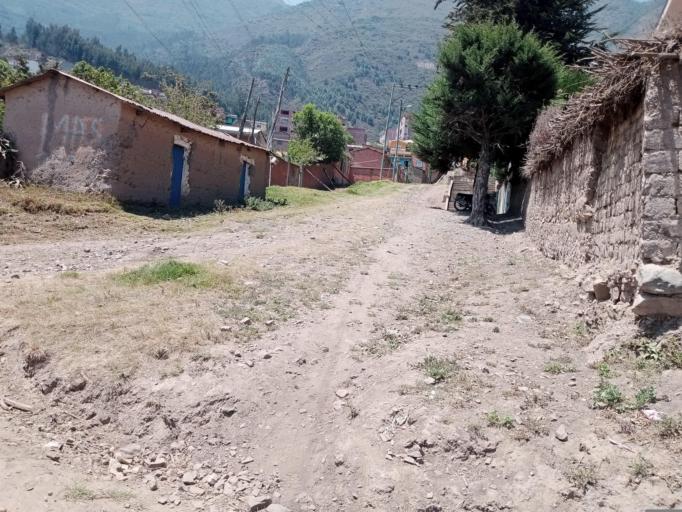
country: BO
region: La Paz
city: Quime
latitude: -16.9053
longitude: -67.1366
